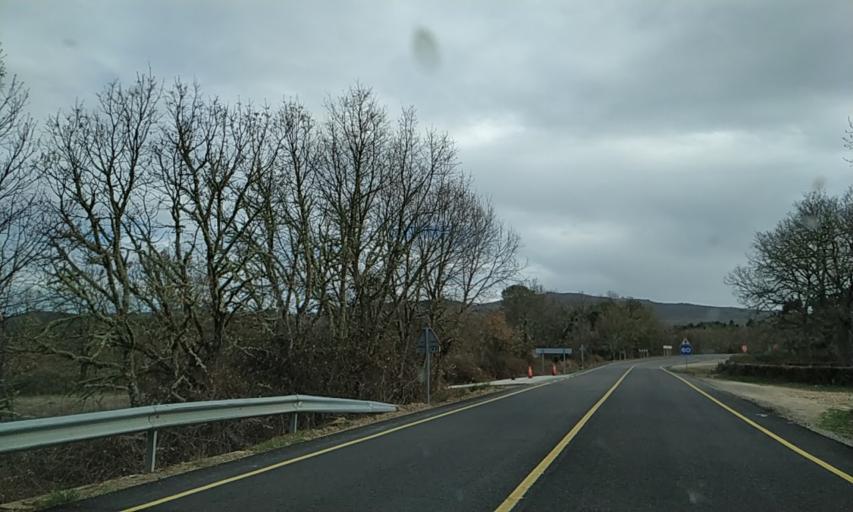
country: ES
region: Castille and Leon
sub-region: Provincia de Salamanca
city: Penaparda
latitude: 40.3138
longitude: -6.6481
